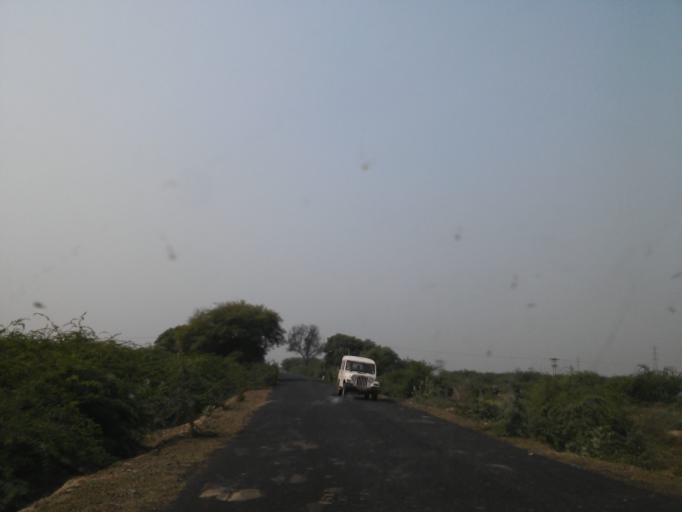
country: IN
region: Gujarat
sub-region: Kachchh
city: Bhuj
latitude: 23.6656
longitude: 69.6437
